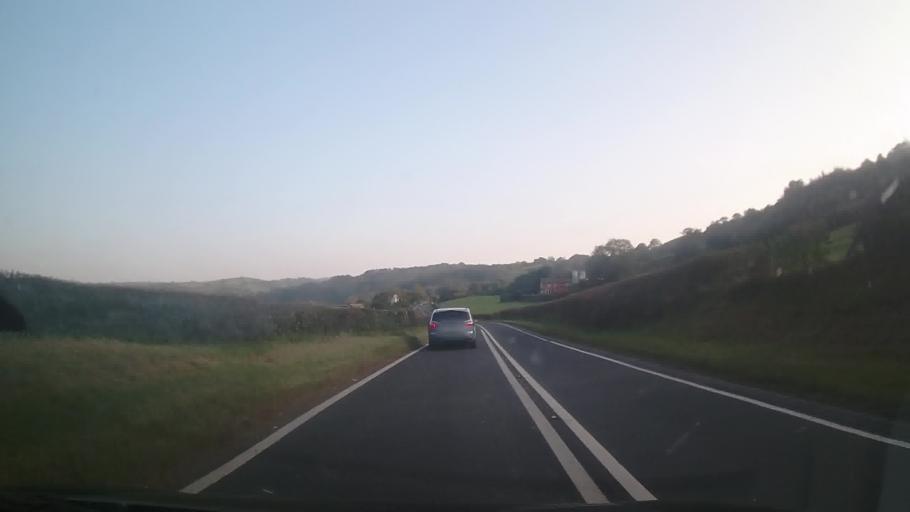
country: GB
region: Wales
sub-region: Sir Powys
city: Mochdre
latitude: 52.5125
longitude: -3.3717
